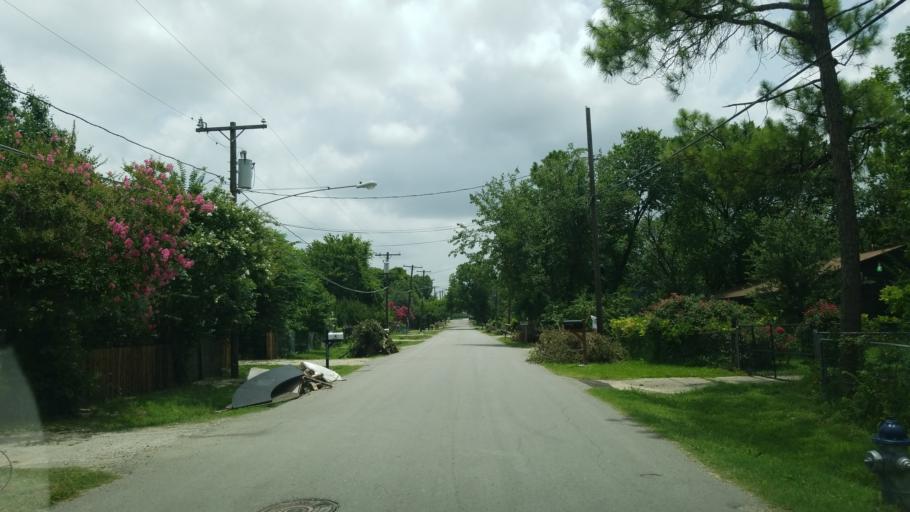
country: US
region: Texas
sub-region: Dallas County
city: Cockrell Hill
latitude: 32.7823
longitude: -96.8989
